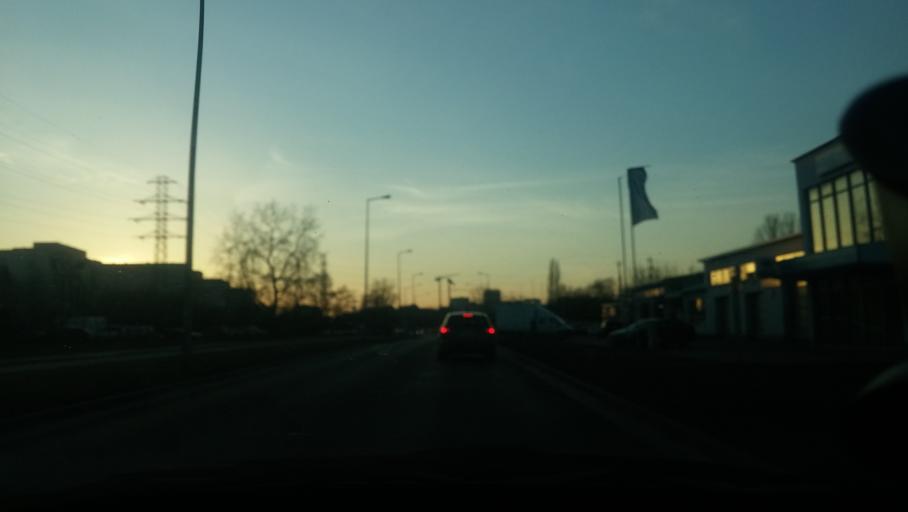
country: PL
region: Masovian Voivodeship
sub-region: Warszawa
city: Praga Poludnie
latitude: 52.2309
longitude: 21.0988
